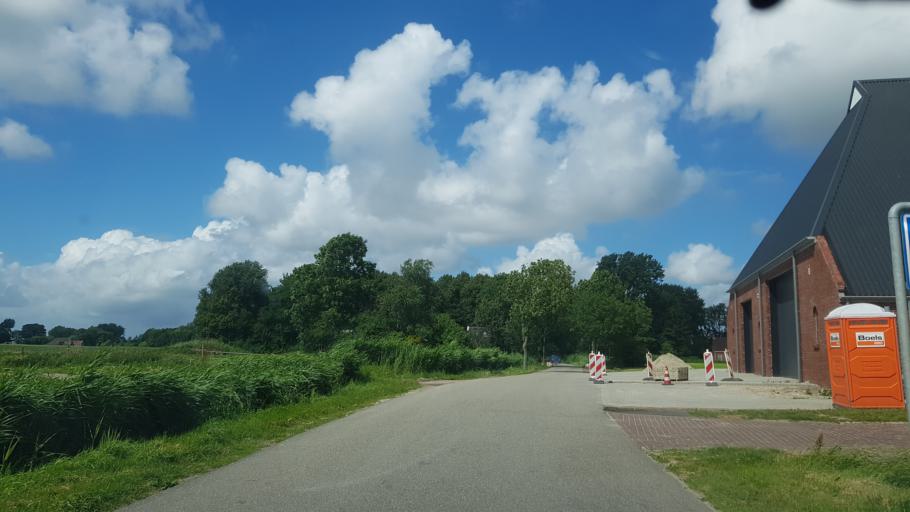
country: NL
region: Groningen
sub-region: Gemeente Winsum
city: Winsum
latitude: 53.3991
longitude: 6.4758
